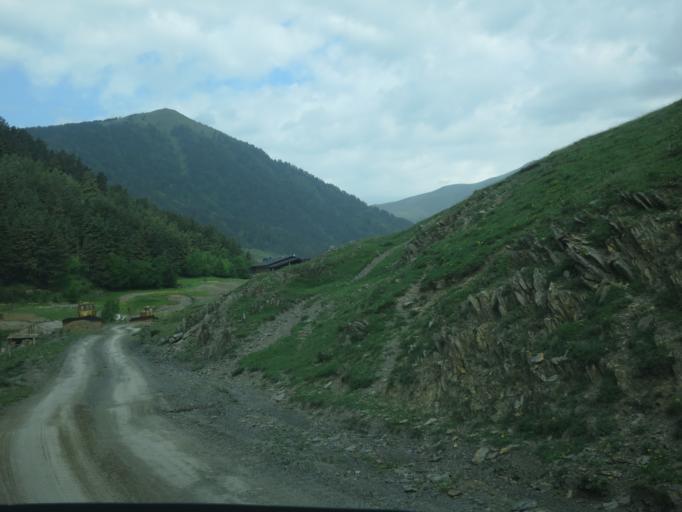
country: RU
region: Chechnya
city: Itum-Kali
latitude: 42.3743
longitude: 45.6322
